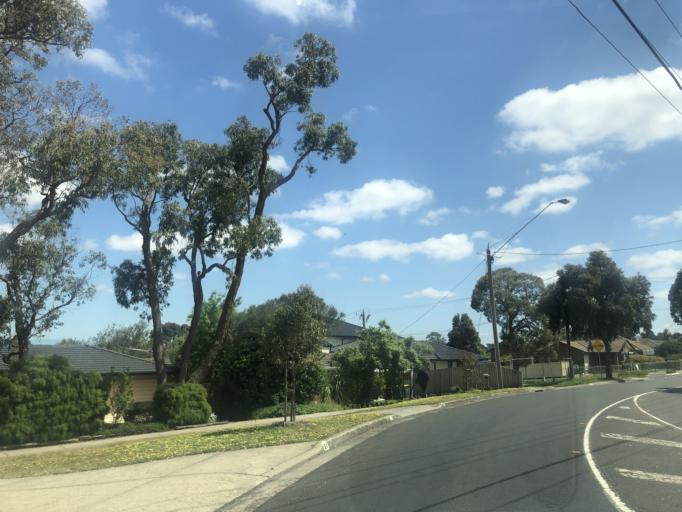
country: AU
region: Victoria
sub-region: Monash
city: Mulgrave
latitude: -37.9115
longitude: 145.1874
